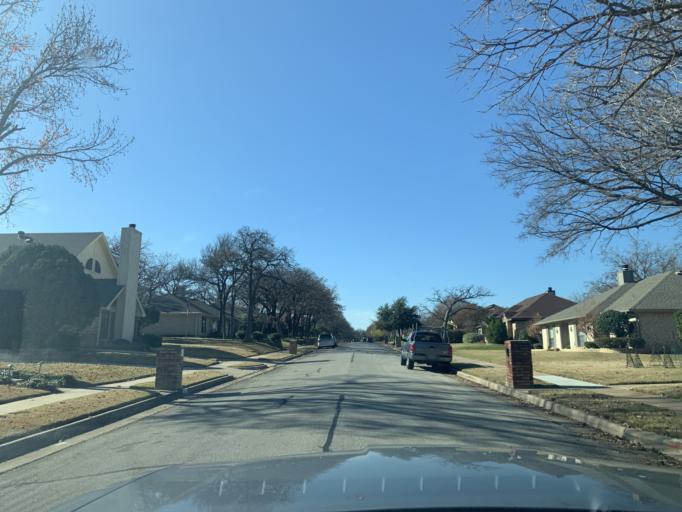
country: US
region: Texas
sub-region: Tarrant County
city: Bedford
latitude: 32.8434
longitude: -97.1542
